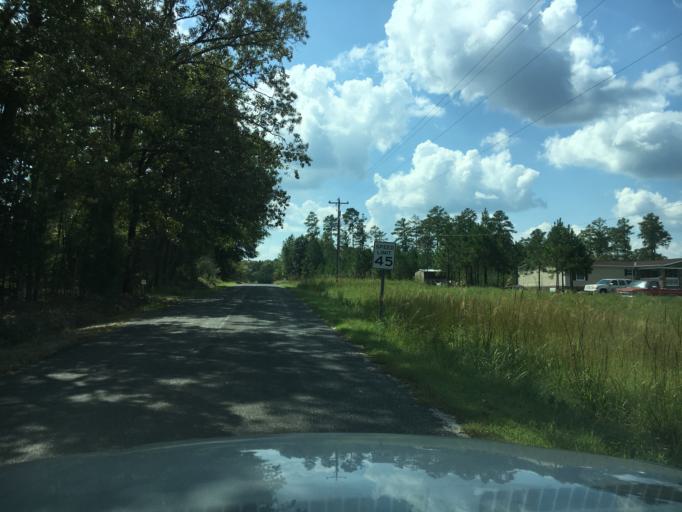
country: US
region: South Carolina
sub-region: Greenwood County
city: Greenwood
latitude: 34.0644
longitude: -82.1452
